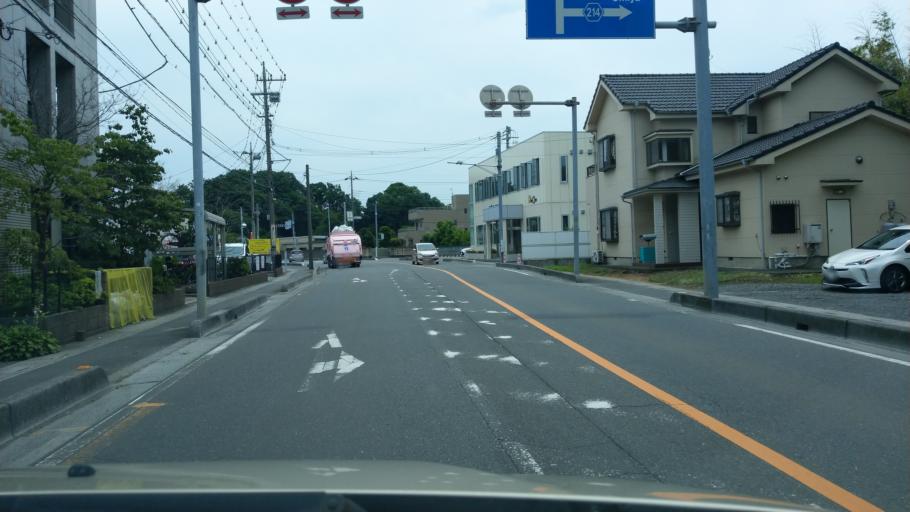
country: JP
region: Saitama
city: Saitama
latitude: 35.9099
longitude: 139.6960
